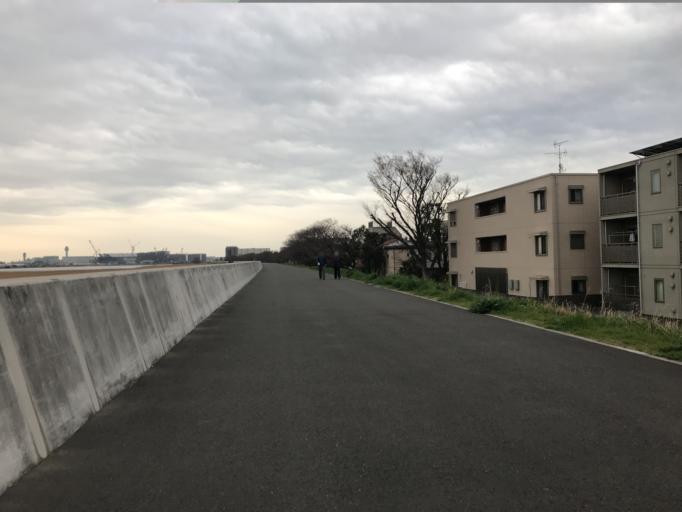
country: JP
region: Kanagawa
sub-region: Kawasaki-shi
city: Kawasaki
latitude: 35.5405
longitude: 139.7441
